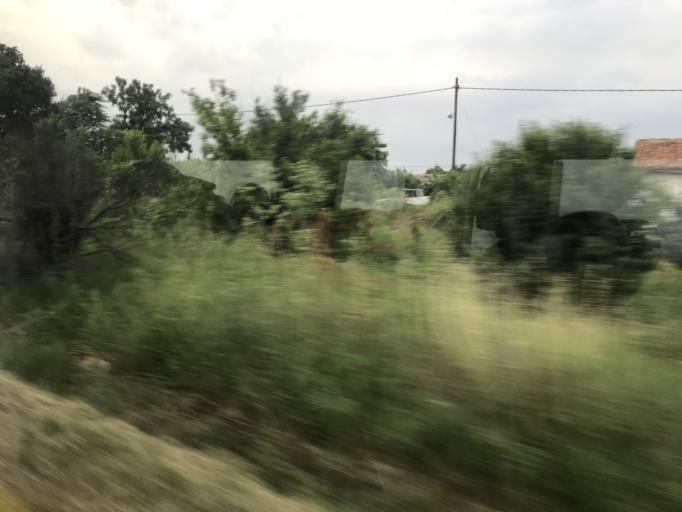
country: GR
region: East Macedonia and Thrace
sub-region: Nomos Rodopis
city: Aratos
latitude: 41.0844
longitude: 25.5372
